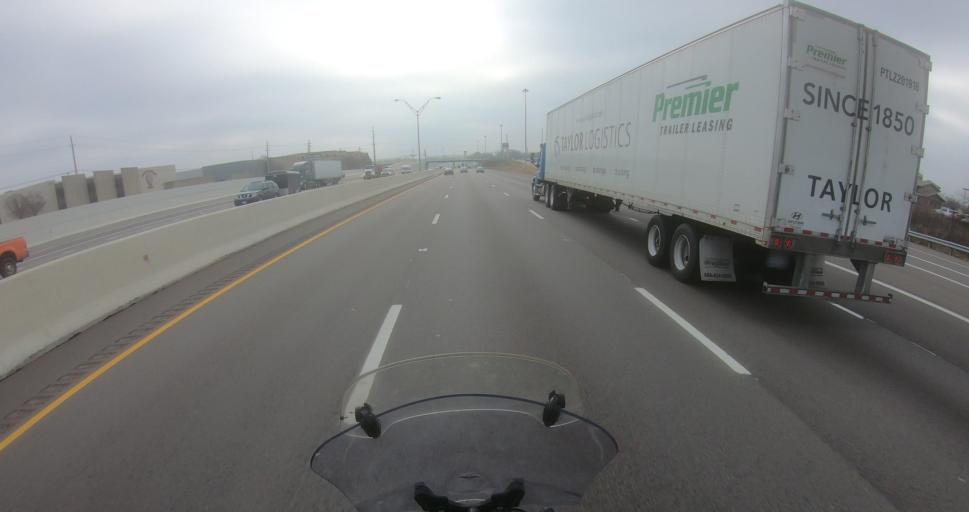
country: US
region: Ohio
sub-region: Montgomery County
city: Northridge
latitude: 39.8458
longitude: -84.1893
